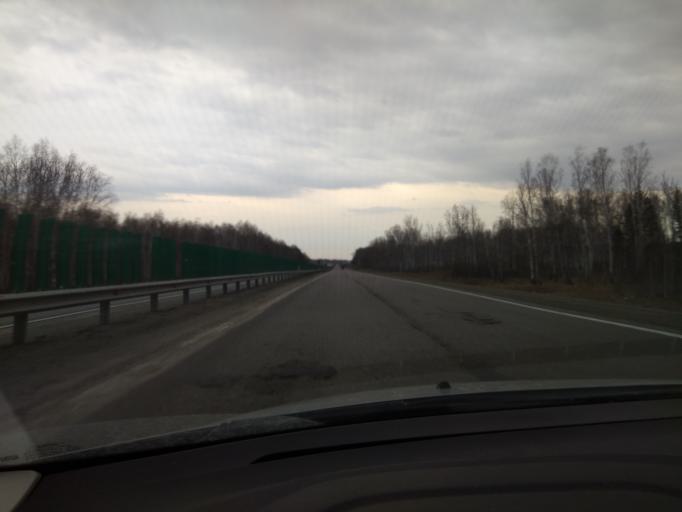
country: RU
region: Chelyabinsk
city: Kunashak
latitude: 55.6255
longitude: 61.2975
